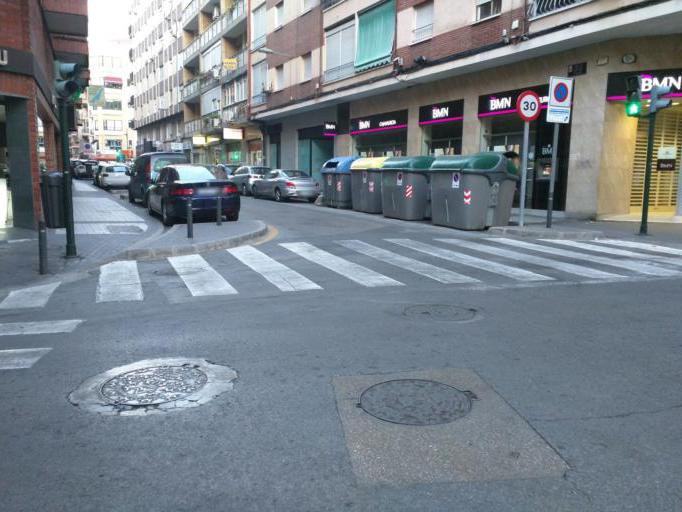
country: ES
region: Murcia
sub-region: Murcia
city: Murcia
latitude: 37.9861
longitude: -1.1240
